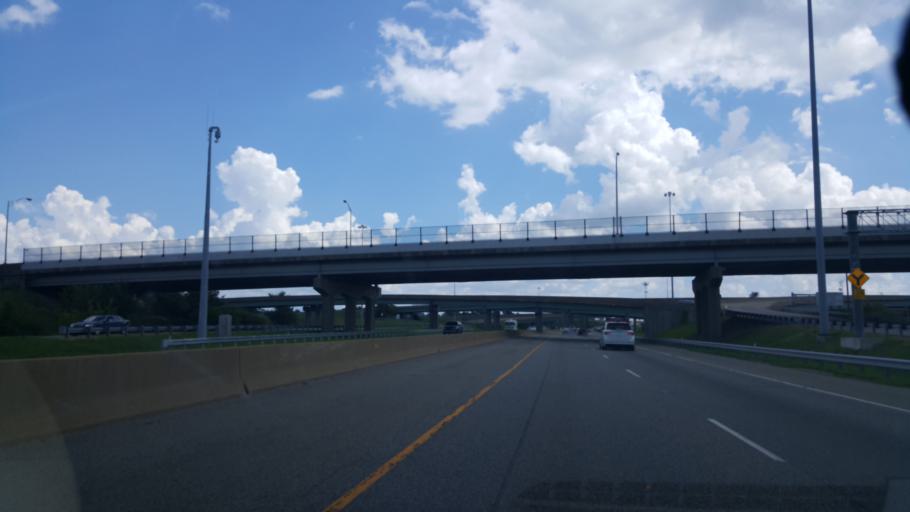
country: US
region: Virginia
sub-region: City of Newport News
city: Newport News
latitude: 36.9826
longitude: -76.4258
